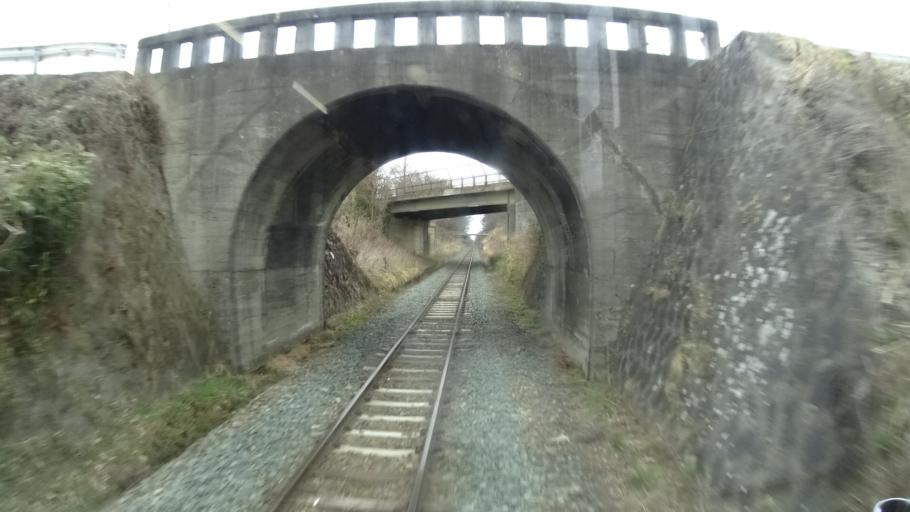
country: JP
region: Iwate
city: Hanamaki
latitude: 39.3898
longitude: 141.2219
